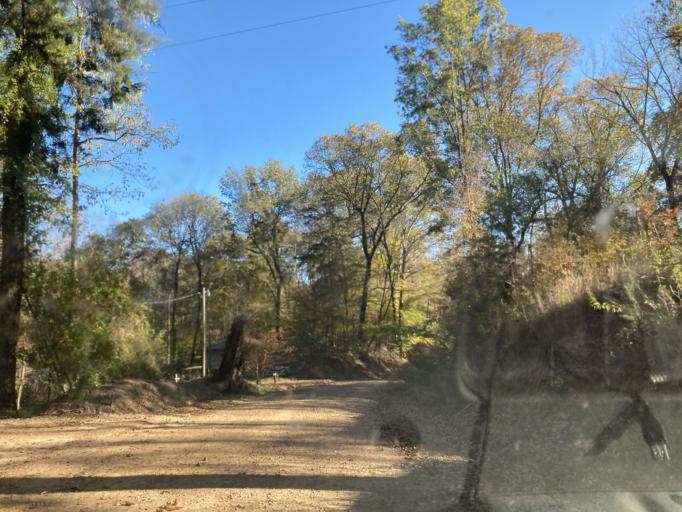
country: US
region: Mississippi
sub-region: Yazoo County
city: Yazoo City
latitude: 32.7450
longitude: -90.4339
